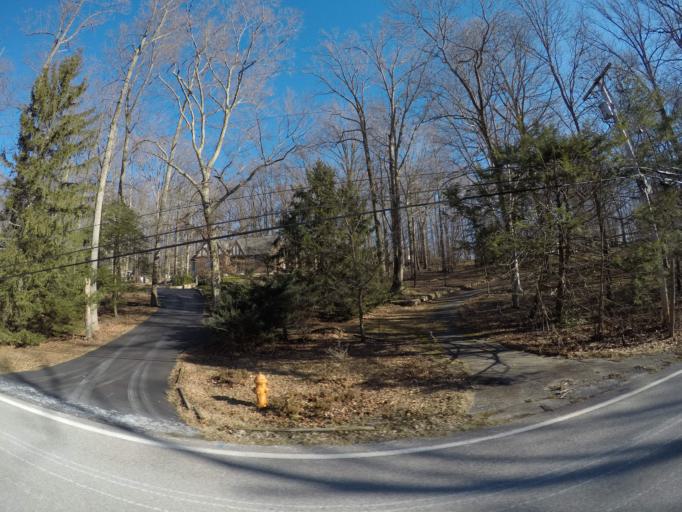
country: US
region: Maryland
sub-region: Howard County
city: Ilchester
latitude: 39.2346
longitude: -76.7820
